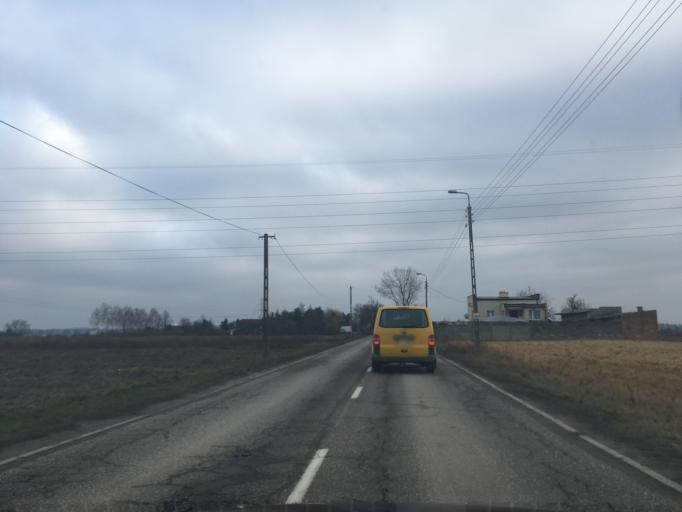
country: PL
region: Masovian Voivodeship
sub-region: Powiat piaseczynski
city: Lesznowola
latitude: 52.0900
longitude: 20.9709
